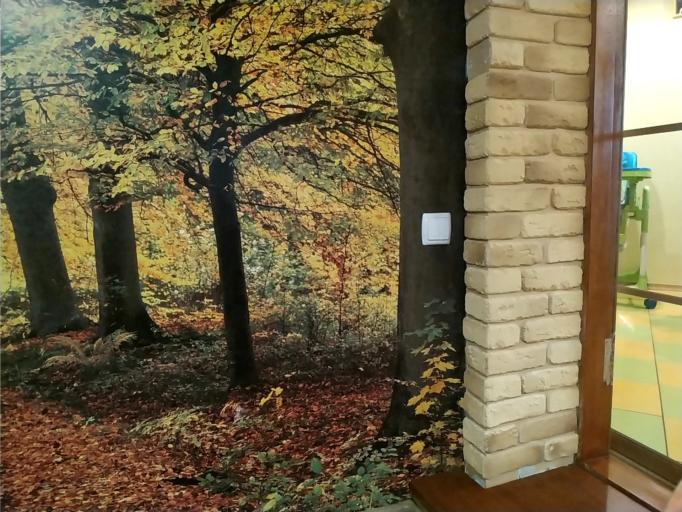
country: RU
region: Smolensk
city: Safonovo
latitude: 55.1952
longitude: 33.1462
